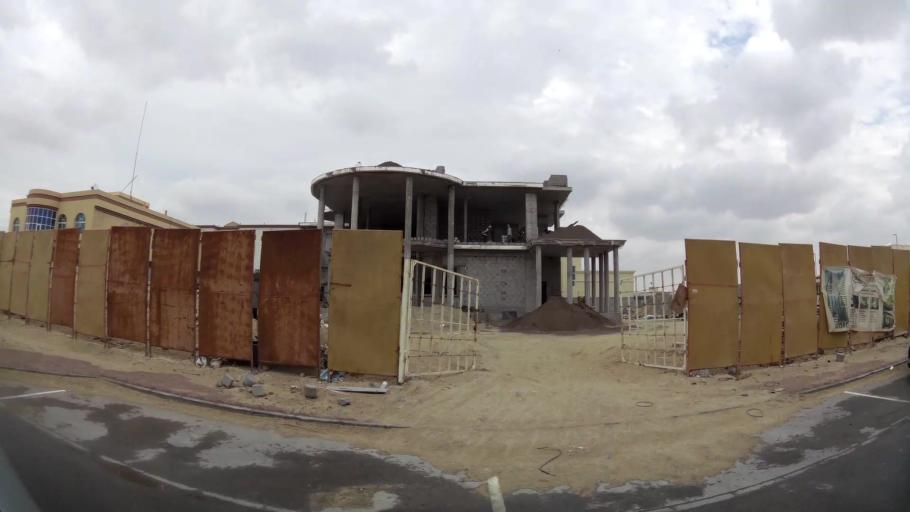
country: AE
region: Abu Dhabi
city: Abu Dhabi
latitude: 24.3525
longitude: 54.6312
